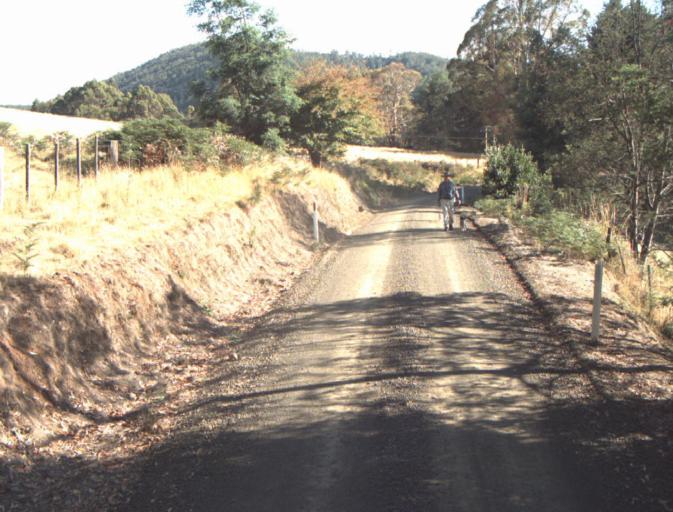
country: AU
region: Tasmania
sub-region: Launceston
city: Mayfield
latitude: -41.2967
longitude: 147.1981
